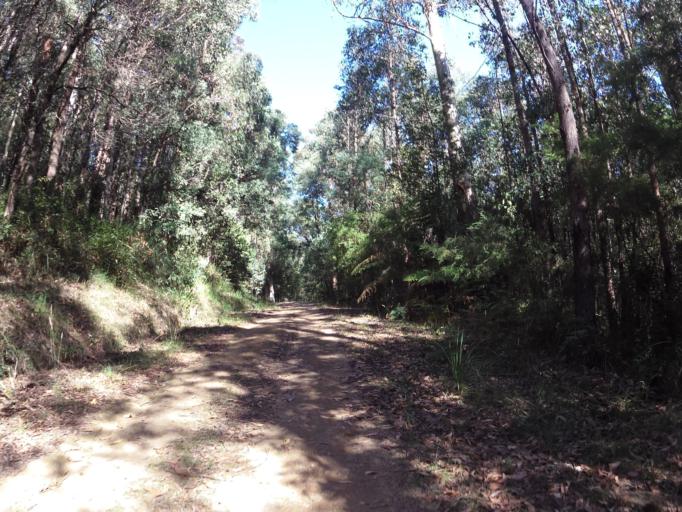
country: AU
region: Victoria
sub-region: Yarra Ranges
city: Millgrove
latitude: -37.8568
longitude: 145.7921
